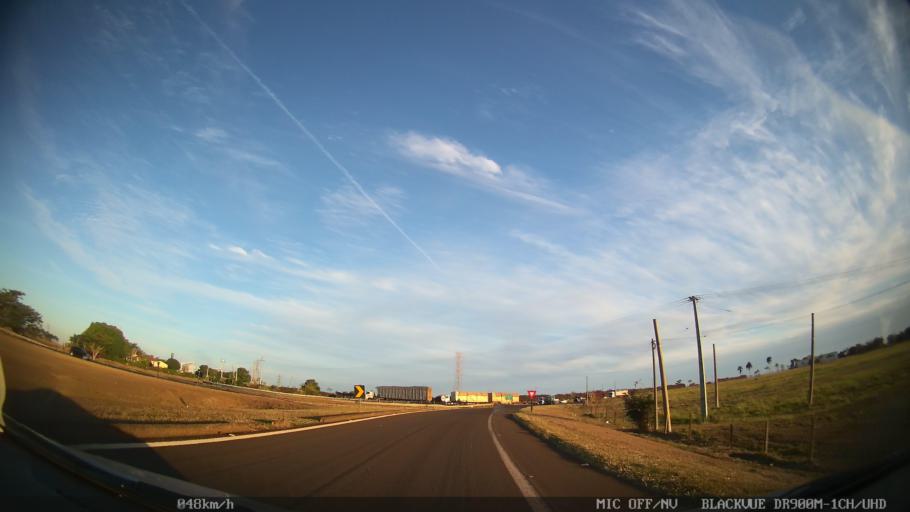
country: BR
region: Sao Paulo
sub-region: Catanduva
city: Catanduva
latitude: -21.1345
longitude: -49.0213
